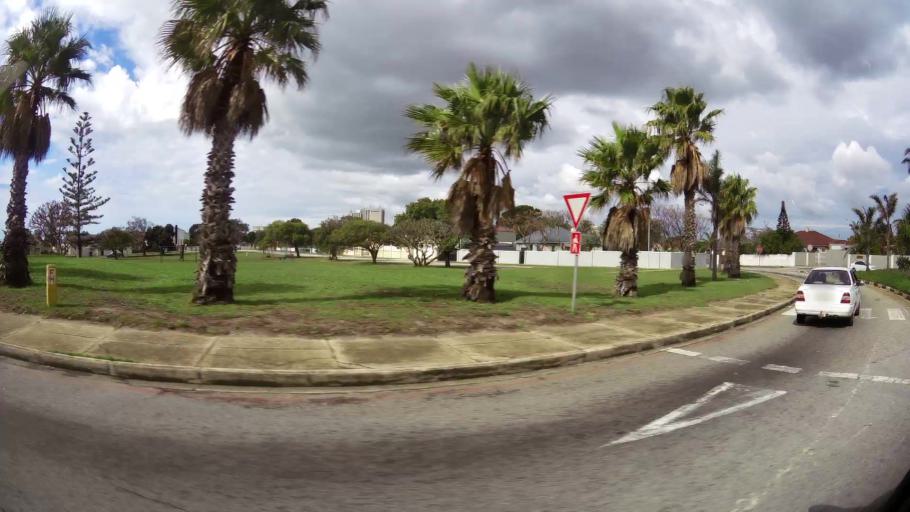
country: ZA
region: Eastern Cape
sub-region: Nelson Mandela Bay Metropolitan Municipality
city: Port Elizabeth
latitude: -33.9560
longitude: 25.5955
